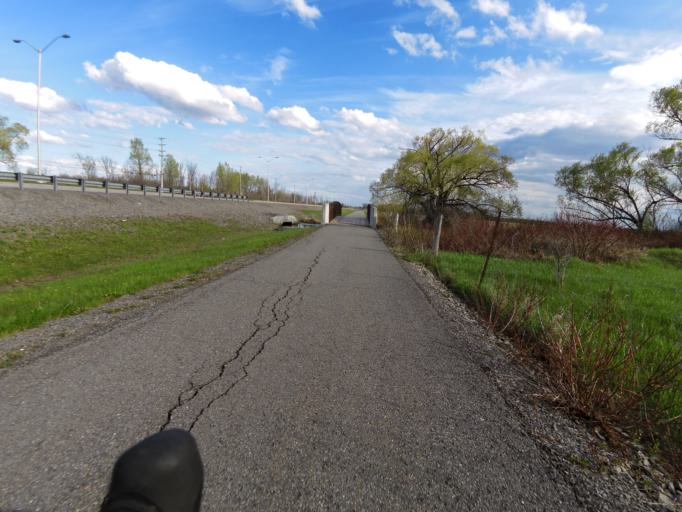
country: CA
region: Ontario
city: Ottawa
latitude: 45.3086
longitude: -75.6834
